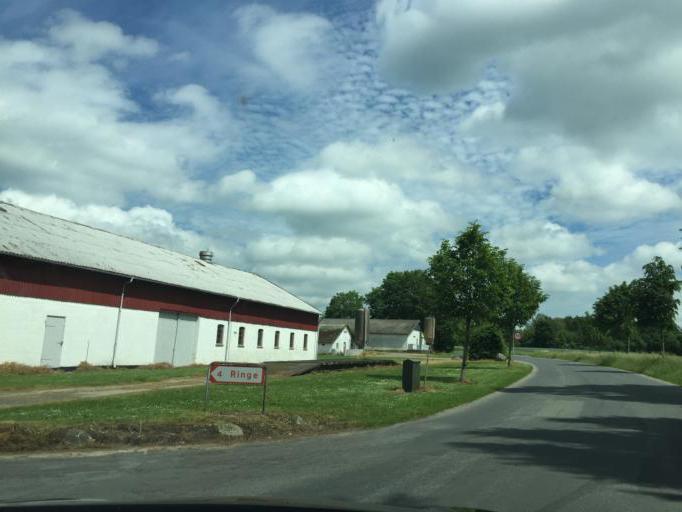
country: DK
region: South Denmark
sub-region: Faaborg-Midtfyn Kommune
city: Ringe
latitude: 55.1958
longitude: 10.4956
